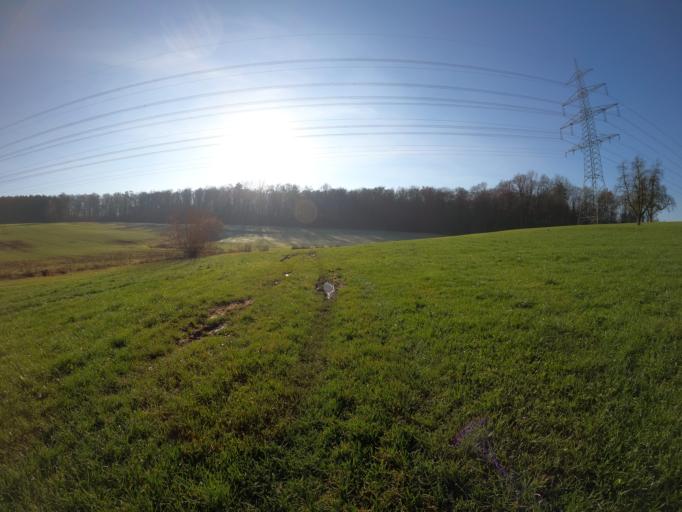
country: DE
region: Baden-Wuerttemberg
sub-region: Regierungsbezirk Stuttgart
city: Albershausen
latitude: 48.7038
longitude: 9.5524
